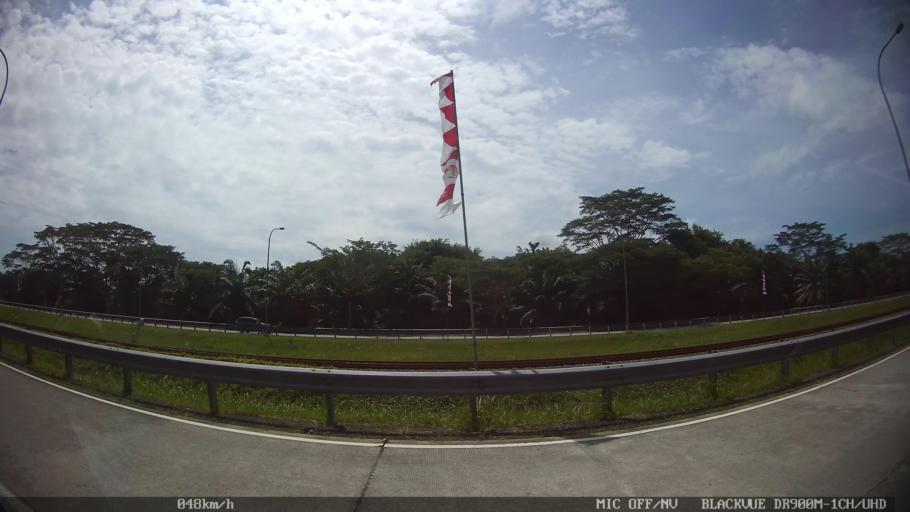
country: ID
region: North Sumatra
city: Percut
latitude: 3.6188
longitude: 98.8623
